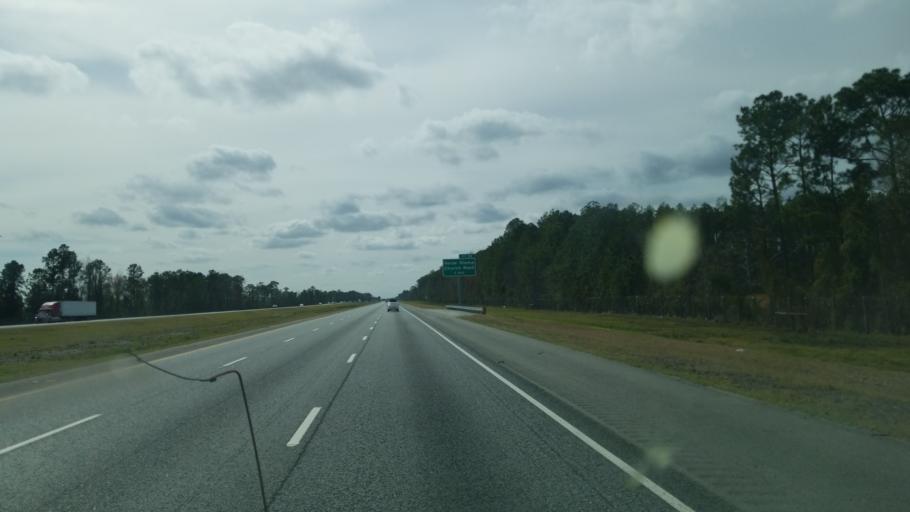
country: US
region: Georgia
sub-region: Camden County
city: Woodbine
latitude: 31.0737
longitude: -81.6227
